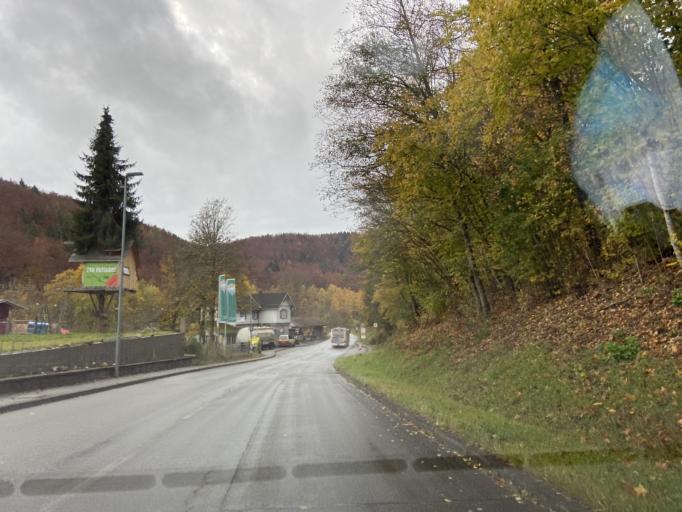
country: DE
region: Baden-Wuerttemberg
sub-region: Tuebingen Region
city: Stetten am Kalten Markt
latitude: 48.0864
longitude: 9.0959
